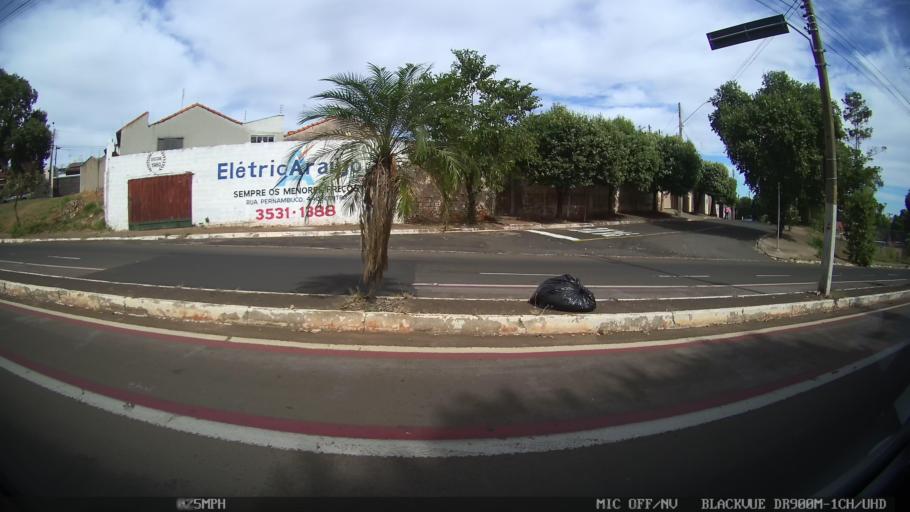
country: BR
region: Sao Paulo
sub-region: Catanduva
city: Catanduva
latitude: -21.1438
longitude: -48.9475
